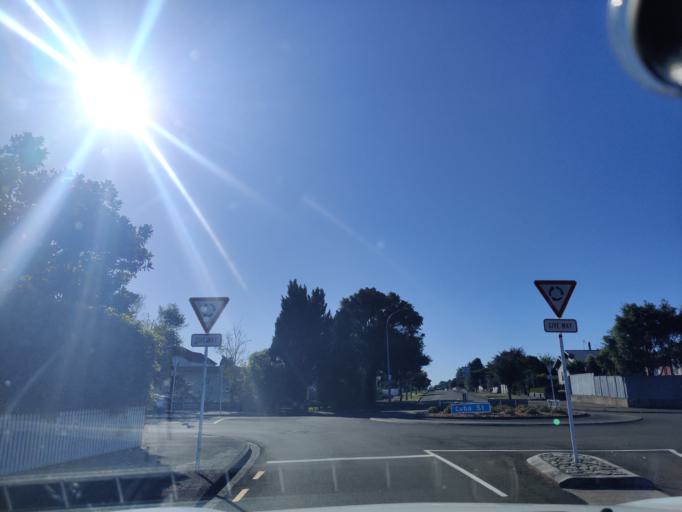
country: NZ
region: Manawatu-Wanganui
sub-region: Palmerston North City
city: Palmerston North
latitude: -40.3601
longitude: 175.5981
